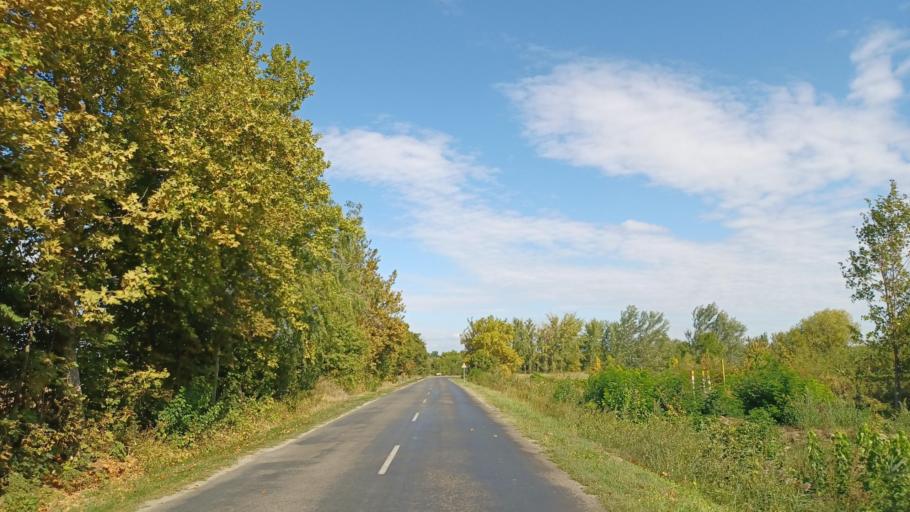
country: HU
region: Tolna
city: Dunaszentgyorgy
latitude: 46.5198
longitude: 18.8263
